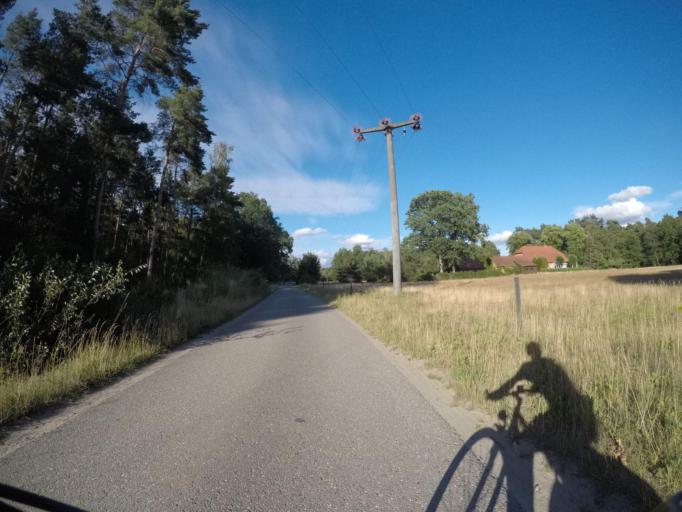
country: DE
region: Mecklenburg-Vorpommern
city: Lubtheen
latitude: 53.2371
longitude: 11.0330
